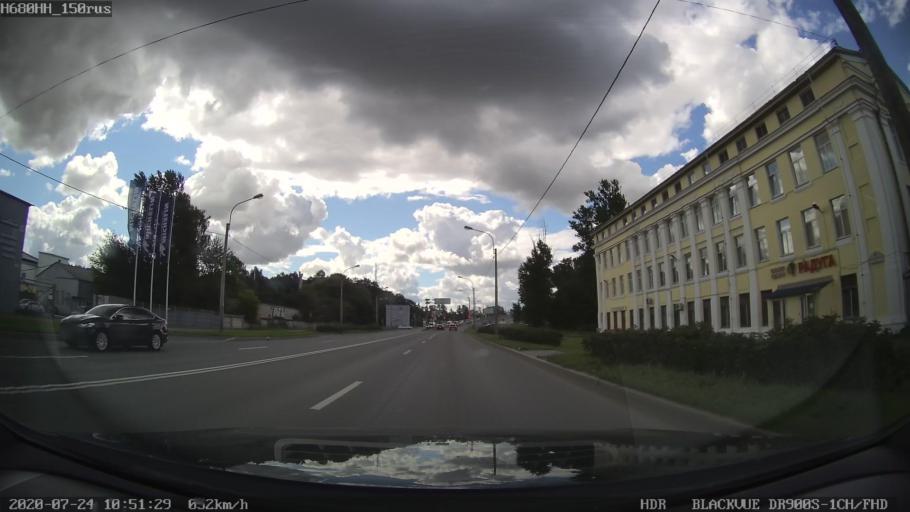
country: RU
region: St.-Petersburg
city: Admiralteisky
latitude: 59.8908
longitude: 30.3019
